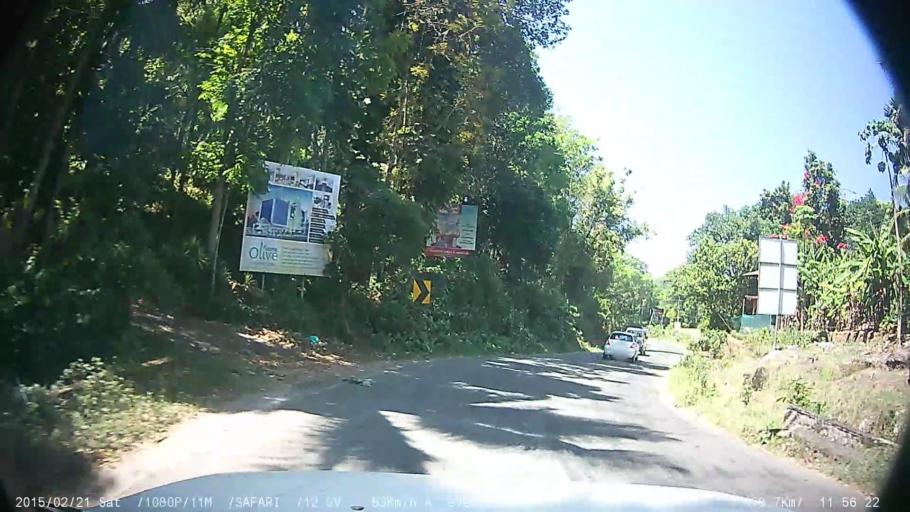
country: IN
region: Kerala
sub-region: Kottayam
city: Lalam
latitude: 9.7411
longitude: 76.6935
